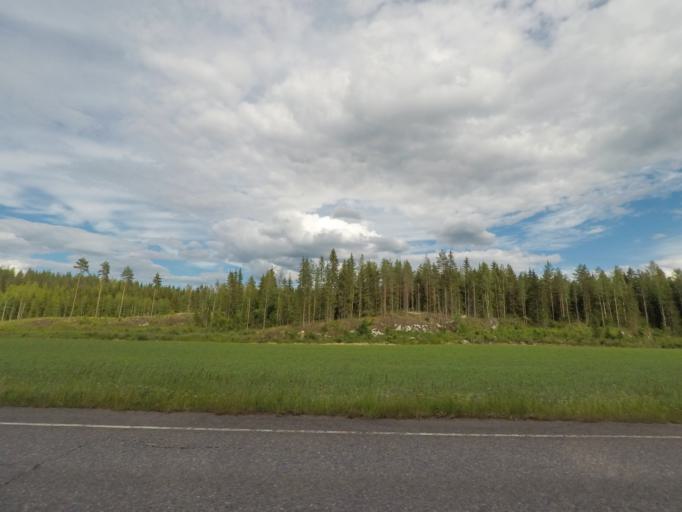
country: FI
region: Paijanne Tavastia
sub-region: Lahti
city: Hollola
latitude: 60.8380
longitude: 25.4932
